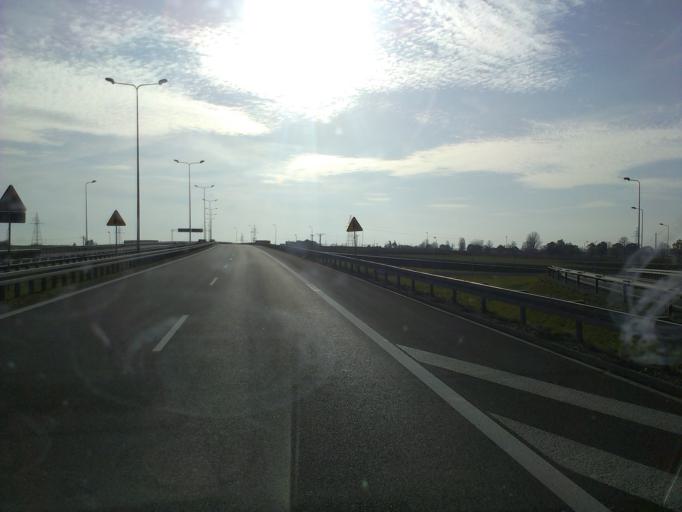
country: PL
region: Lubusz
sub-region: Powiat swiebodzinski
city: Swiebodzin
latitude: 52.2764
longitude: 15.5390
